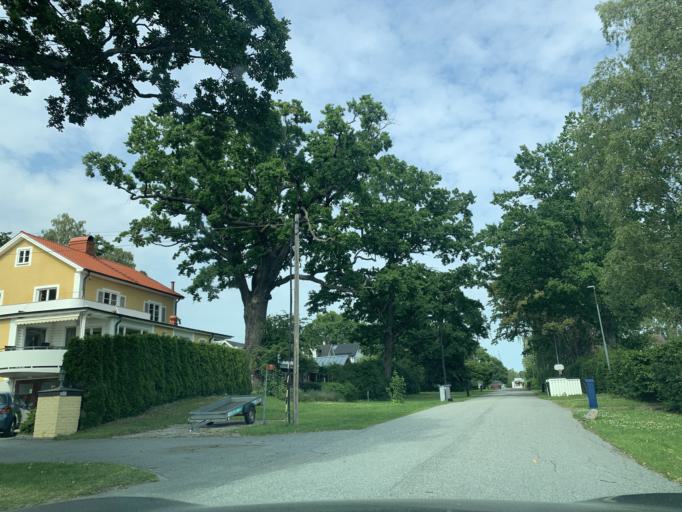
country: SE
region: Stockholm
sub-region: Norrtalje Kommun
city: Bergshamra
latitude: 59.4002
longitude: 18.0114
